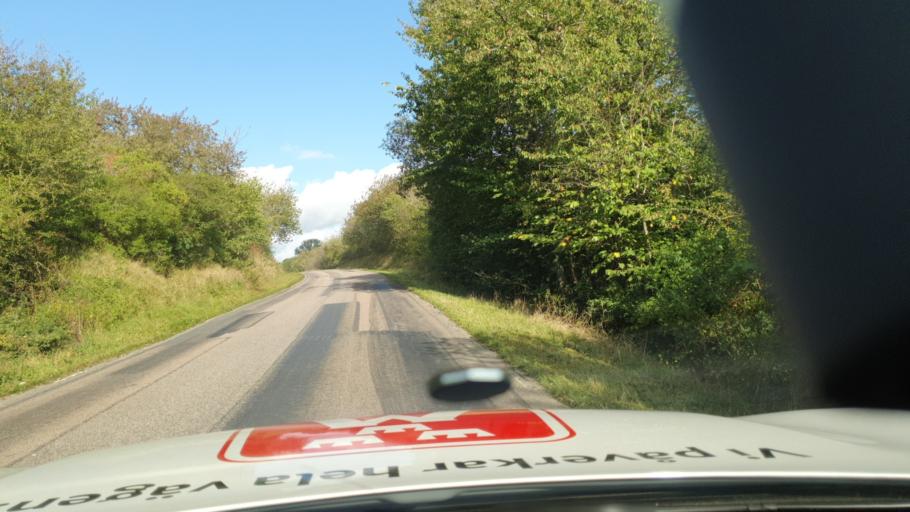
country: SE
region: Skane
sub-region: Tomelilla Kommun
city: Tomelilla
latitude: 55.5286
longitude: 13.9620
